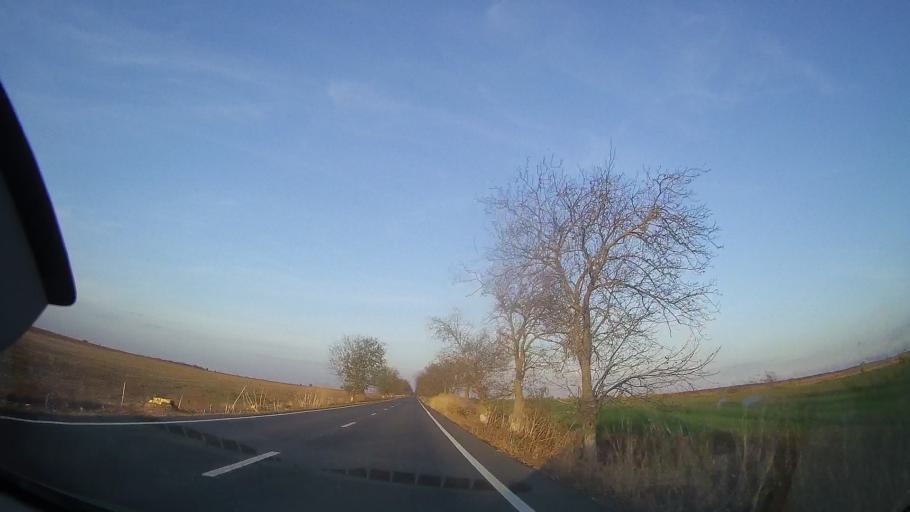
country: RO
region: Constanta
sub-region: Comuna Amzacea
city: Amzacea
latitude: 43.9464
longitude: 28.3774
